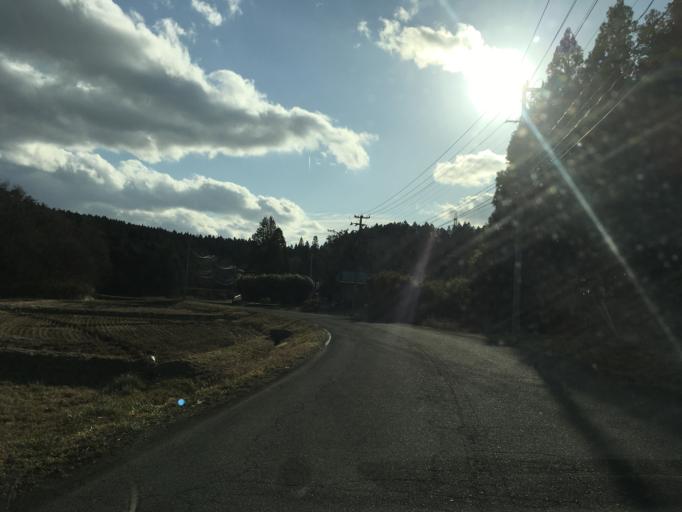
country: JP
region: Iwate
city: Ichinoseki
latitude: 38.8158
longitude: 140.9983
